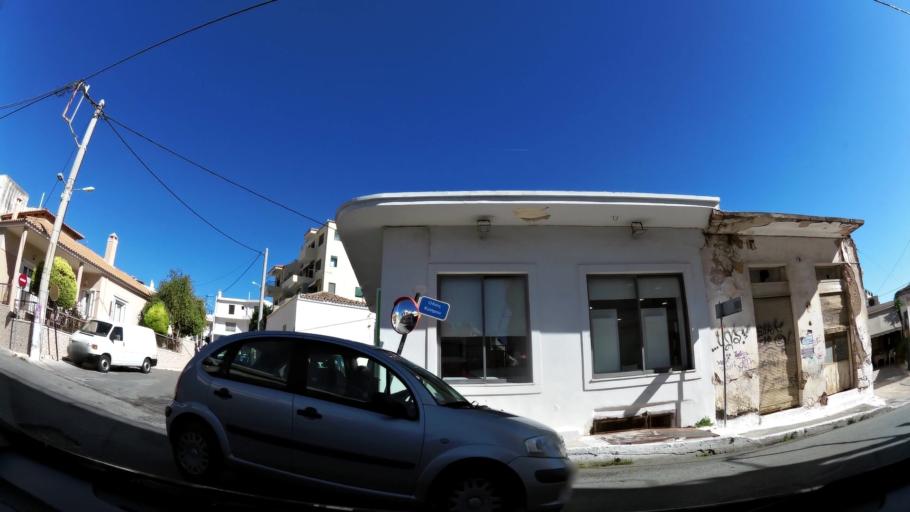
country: GR
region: Attica
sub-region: Nomarchia Anatolikis Attikis
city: Koropi
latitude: 37.8994
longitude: 23.8766
